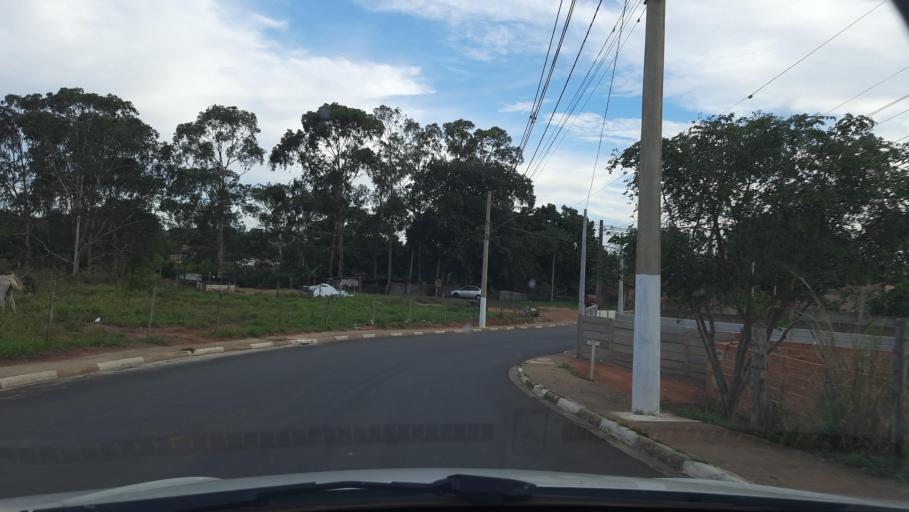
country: BR
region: Sao Paulo
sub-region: Casa Branca
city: Casa Branca
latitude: -21.7637
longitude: -47.0857
